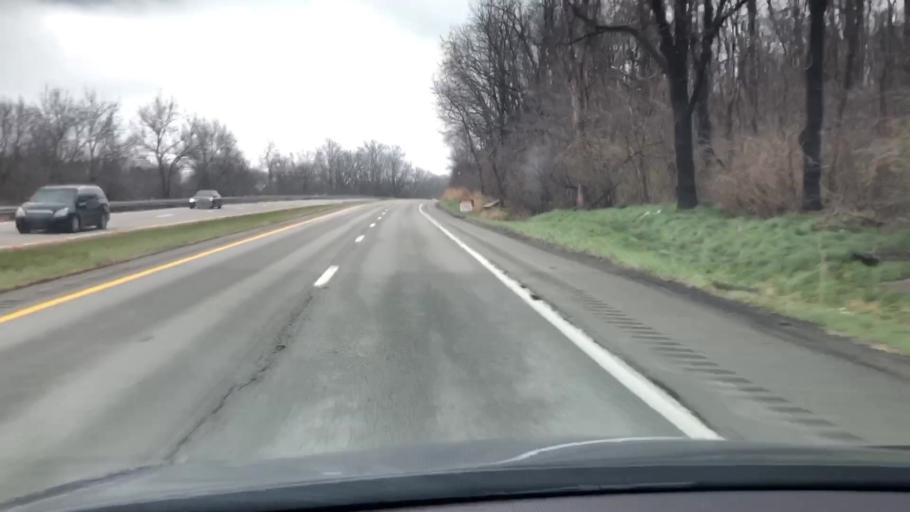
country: US
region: Pennsylvania
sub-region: Westmoreland County
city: Scottdale
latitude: 40.0776
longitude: -79.5626
